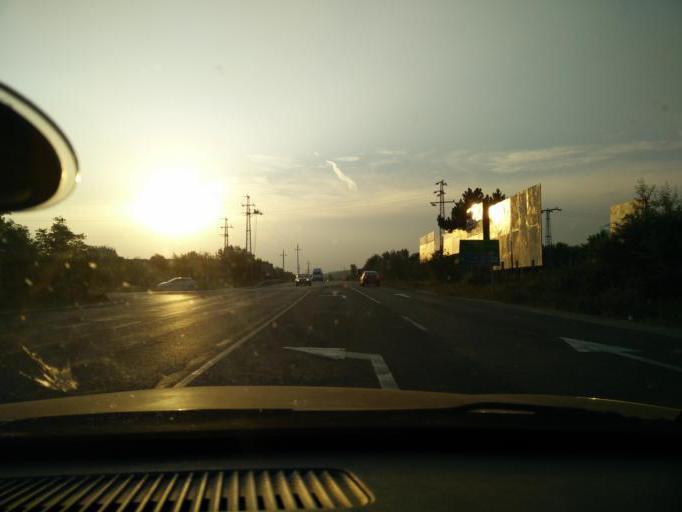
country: HU
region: Pest
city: Toeroekbalint
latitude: 47.4553
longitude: 18.9077
